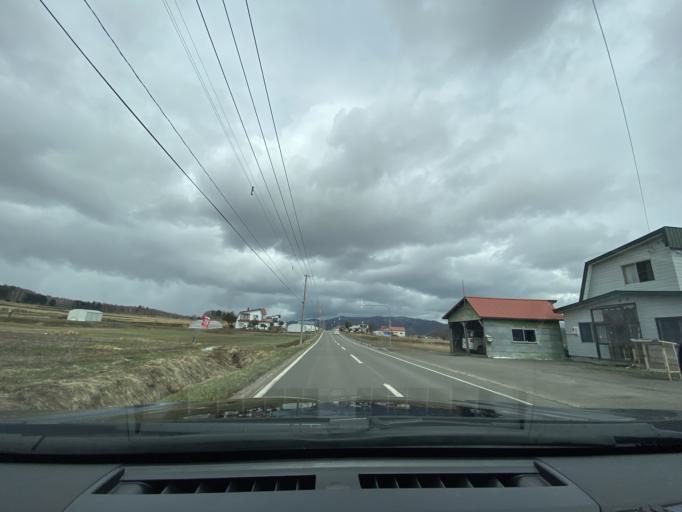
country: JP
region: Hokkaido
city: Nayoro
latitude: 44.0982
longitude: 142.4749
